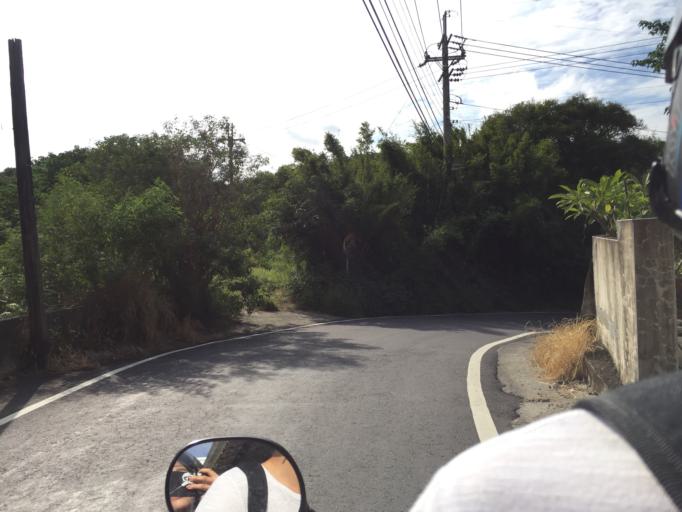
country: TW
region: Taiwan
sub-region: Hsinchu
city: Hsinchu
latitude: 24.7719
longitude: 120.9346
